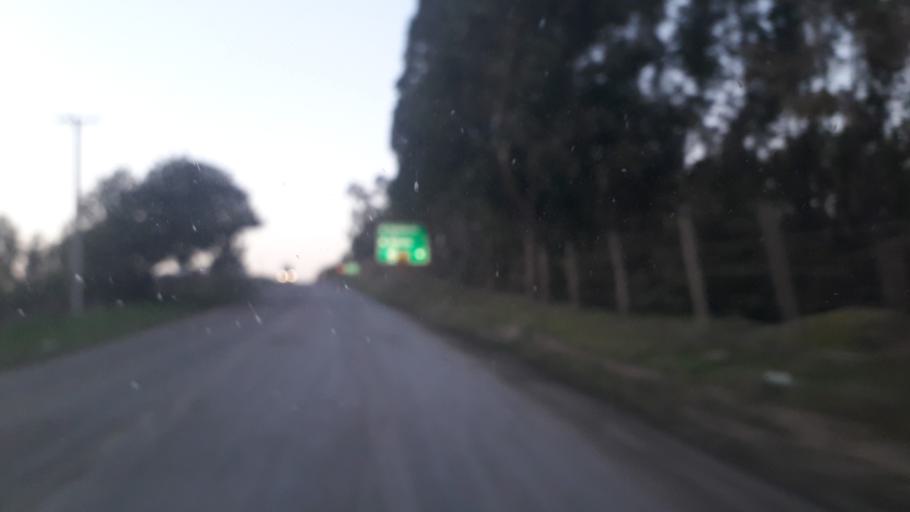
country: CL
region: Valparaiso
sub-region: Provincia de Quillota
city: Hacienda La Calera
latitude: -32.7392
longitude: -71.4176
